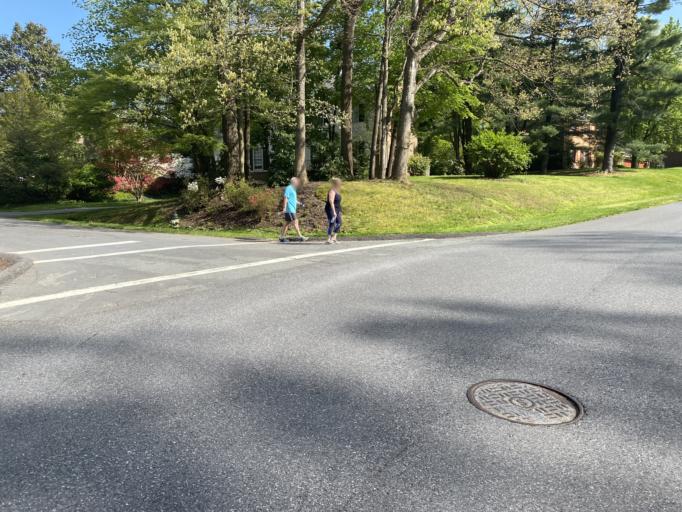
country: US
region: Maryland
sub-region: Montgomery County
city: Potomac
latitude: 39.0503
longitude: -77.2038
